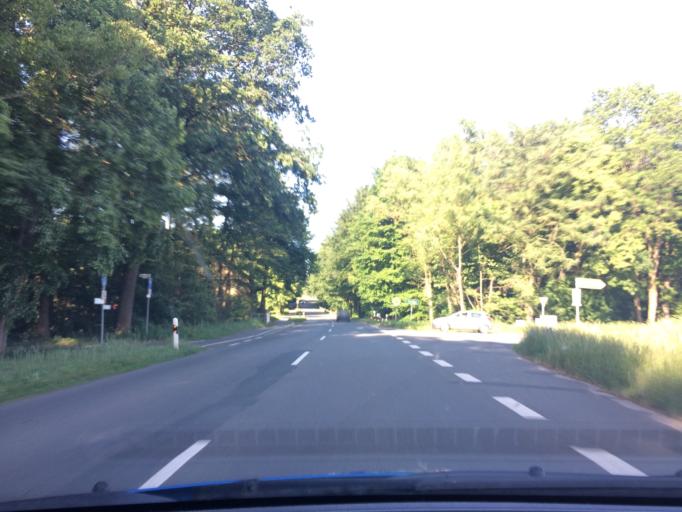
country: DE
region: Lower Saxony
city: Soltau
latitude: 53.0201
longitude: 9.8986
